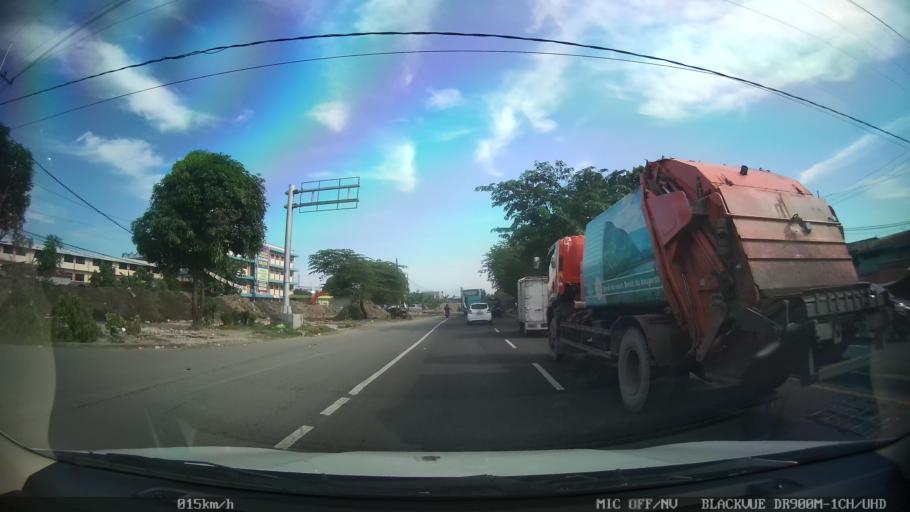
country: ID
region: North Sumatra
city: Sunggal
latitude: 3.6103
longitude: 98.6276
